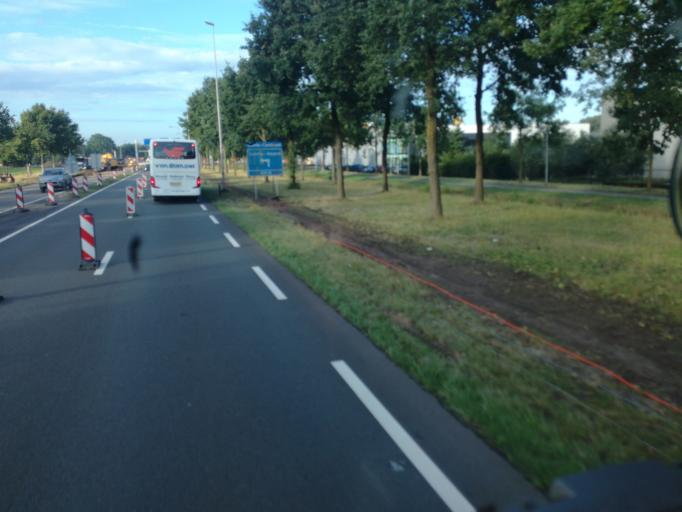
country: NL
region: North Brabant
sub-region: Gemeente Goirle
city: Goirle
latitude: 51.5329
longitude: 5.0453
